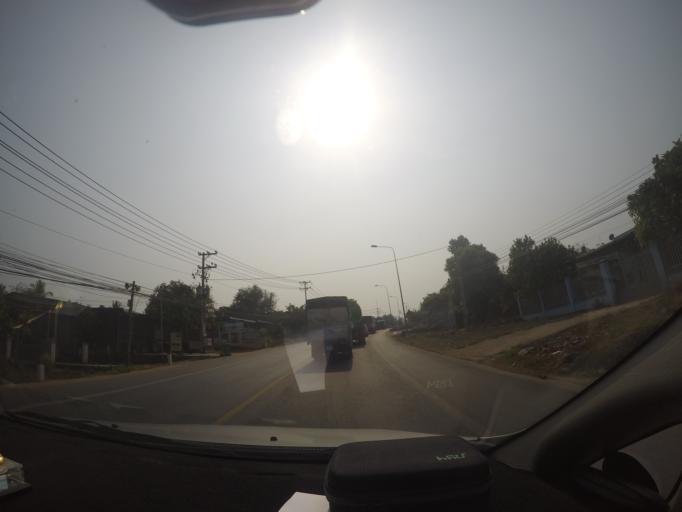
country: VN
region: Dong Nai
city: Tan Phu
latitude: 11.1790
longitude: 107.3357
